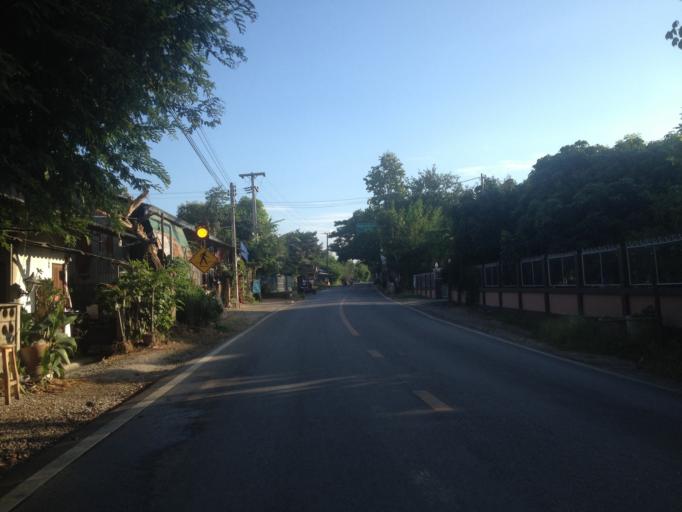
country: TH
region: Chiang Mai
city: San Pa Tong
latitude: 18.5945
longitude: 98.8618
